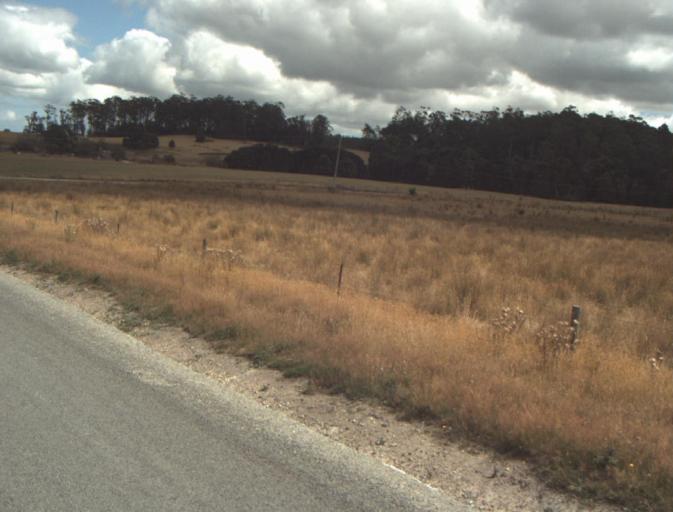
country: AU
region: Tasmania
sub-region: Launceston
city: Mayfield
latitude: -41.1931
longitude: 147.1681
